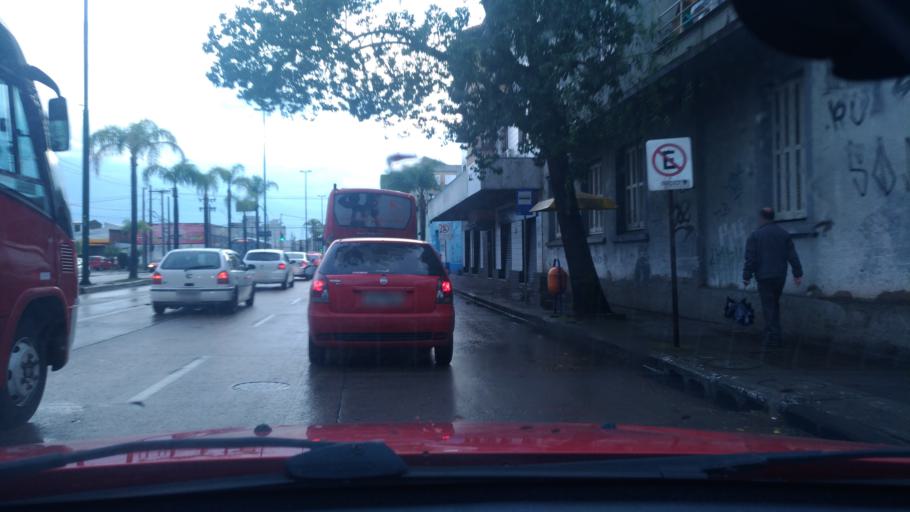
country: BR
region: Rio Grande do Sul
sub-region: Porto Alegre
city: Porto Alegre
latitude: -30.0232
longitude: -51.2131
